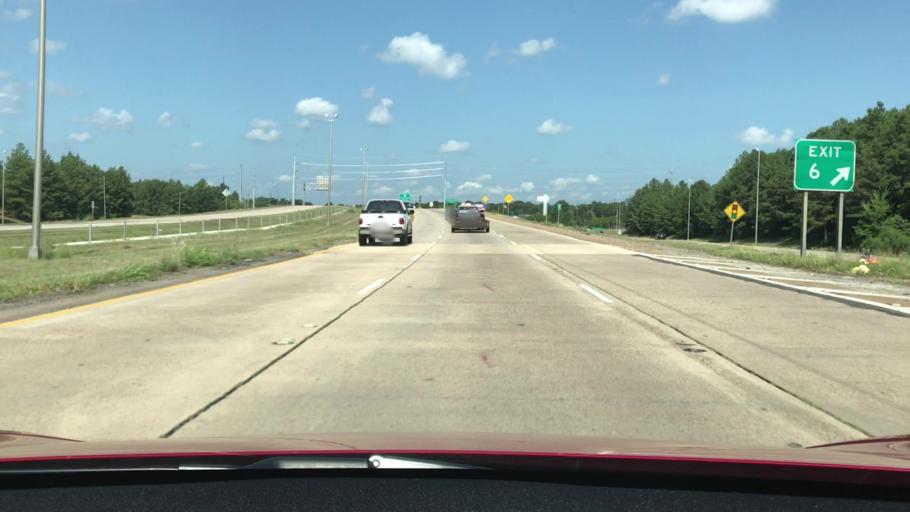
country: US
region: Louisiana
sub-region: Bossier Parish
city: Bossier City
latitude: 32.4205
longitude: -93.7592
